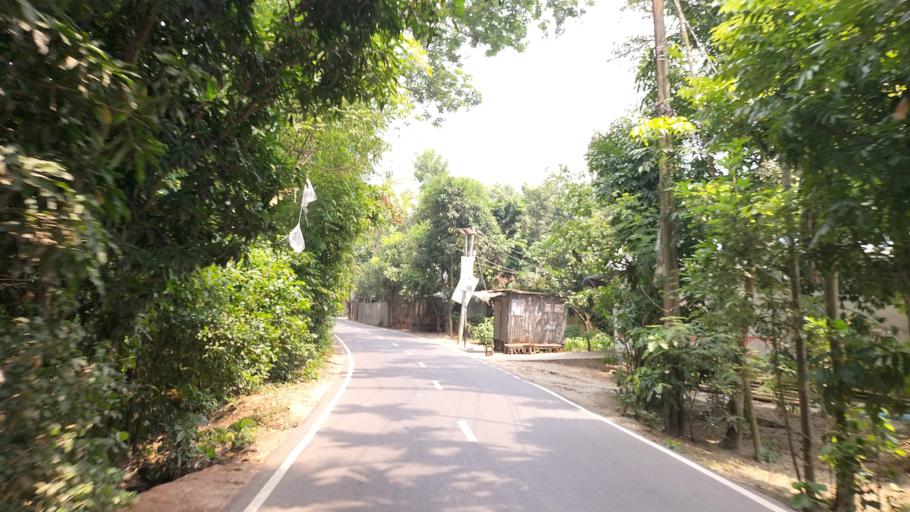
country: BD
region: Dhaka
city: Azimpur
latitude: 23.7154
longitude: 90.2788
